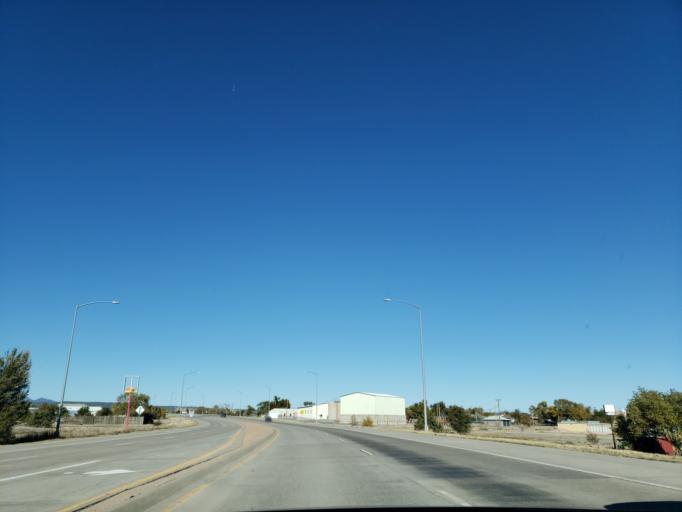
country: US
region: Colorado
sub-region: Fremont County
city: Penrose
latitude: 38.4253
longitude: -105.0274
